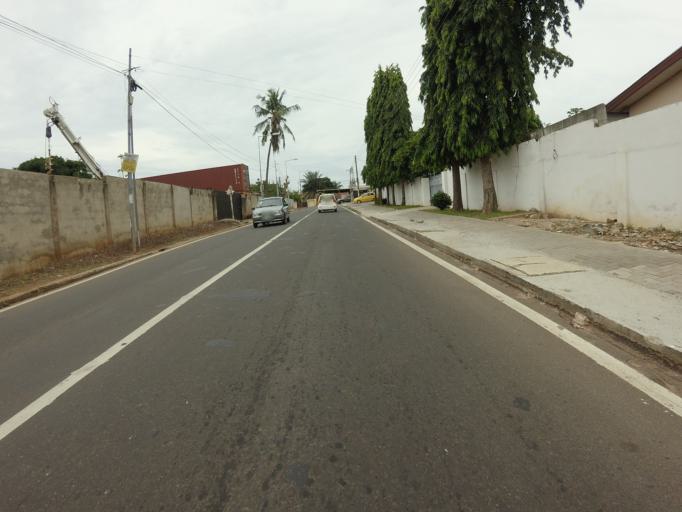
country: GH
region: Greater Accra
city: Dome
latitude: 5.5993
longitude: -0.2304
